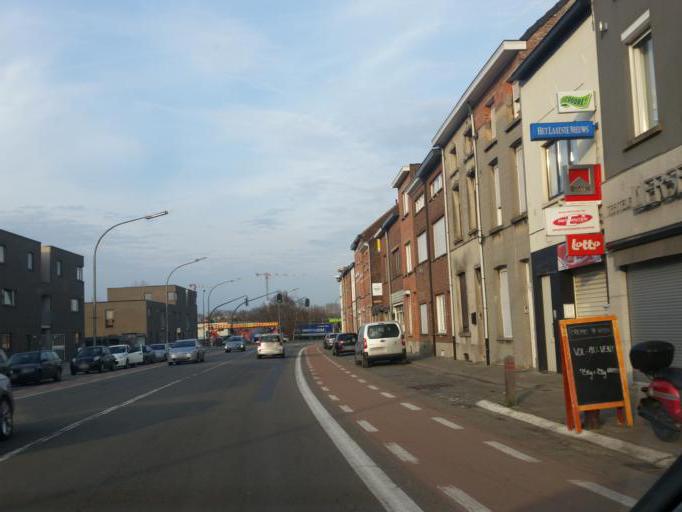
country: BE
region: Flanders
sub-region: Provincie Antwerpen
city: Mechelen
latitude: 51.0427
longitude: 4.4773
